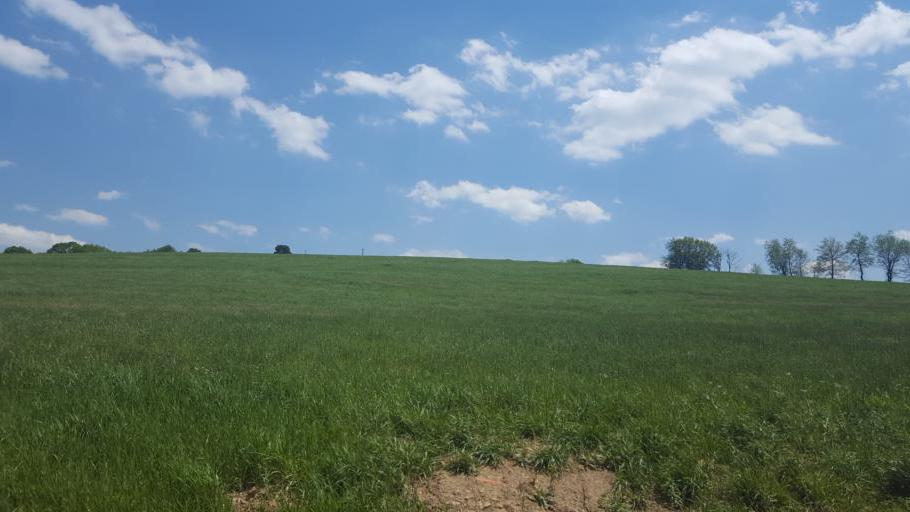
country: US
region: Ohio
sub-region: Knox County
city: Oak Hill
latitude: 40.3002
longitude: -82.2370
